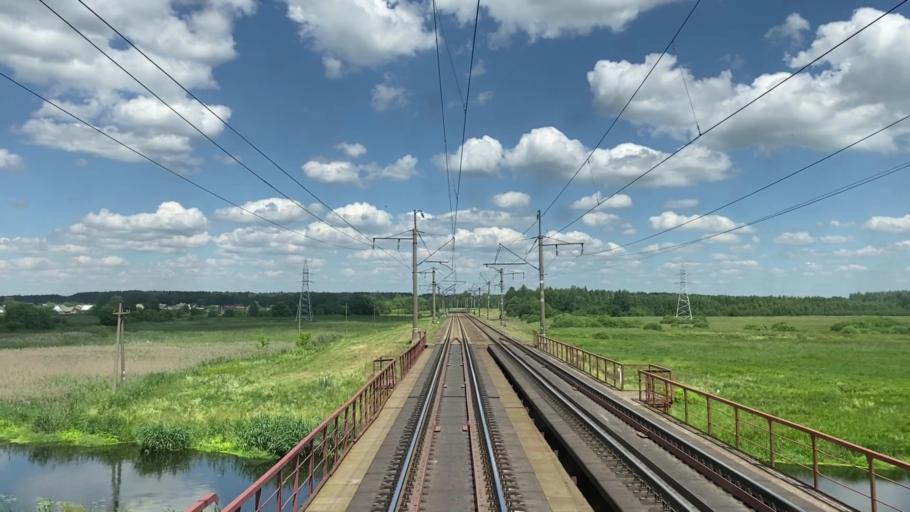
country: BY
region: Brest
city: Ivatsevichy
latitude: 52.7207
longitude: 25.3580
